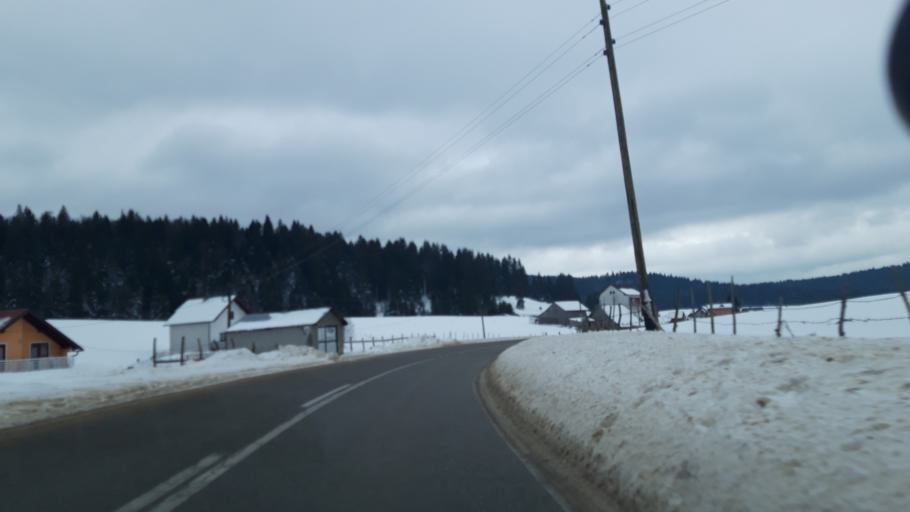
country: BA
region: Republika Srpska
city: Han Pijesak
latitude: 44.1074
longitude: 18.9706
